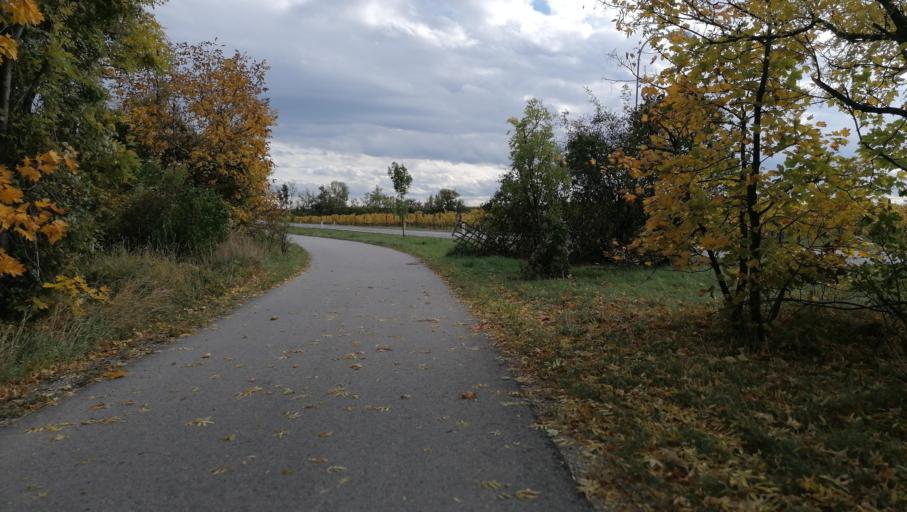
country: AT
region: Lower Austria
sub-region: Politischer Bezirk Baden
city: Tattendorf
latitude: 47.9472
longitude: 16.3139
